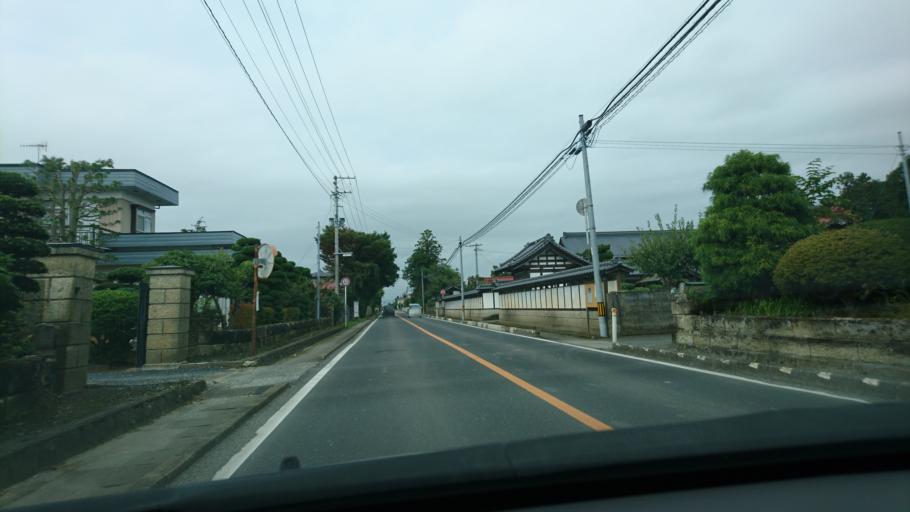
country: JP
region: Iwate
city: Ichinoseki
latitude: 38.7712
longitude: 141.1001
